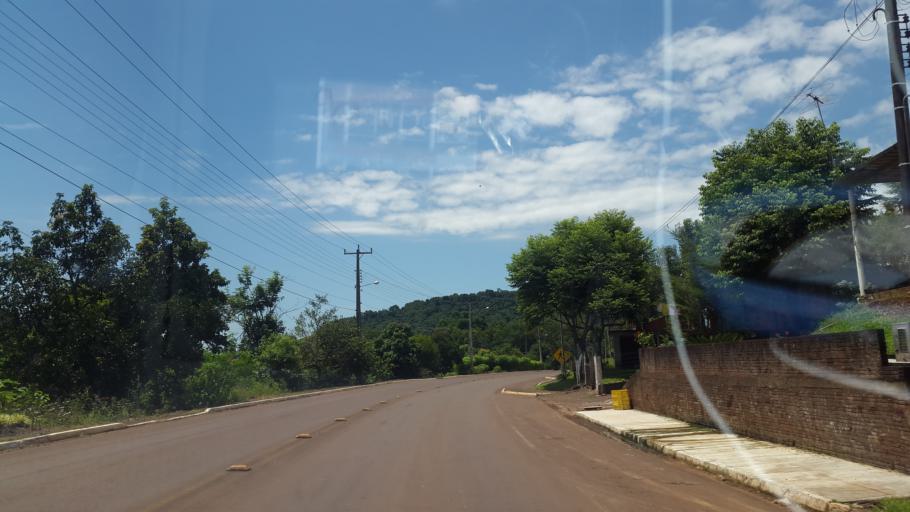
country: BR
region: Rio Grande do Sul
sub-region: Frederico Westphalen
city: Frederico Westphalen
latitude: -27.0666
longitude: -53.4298
